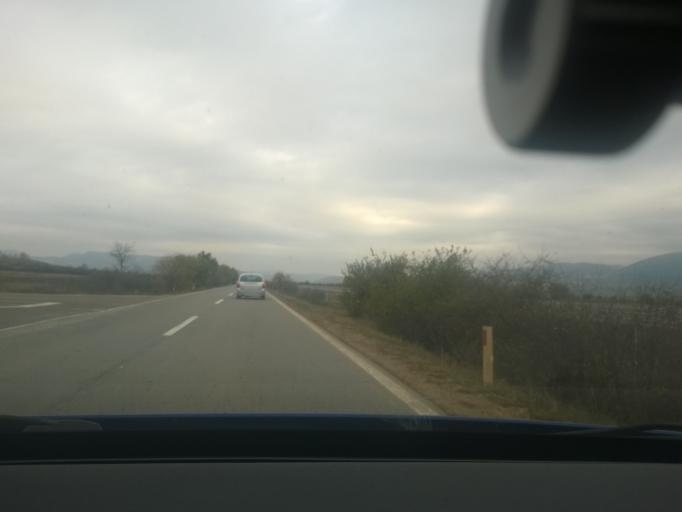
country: RS
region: Central Serbia
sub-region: Pirotski Okrug
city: Pirot
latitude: 43.0958
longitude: 22.6472
